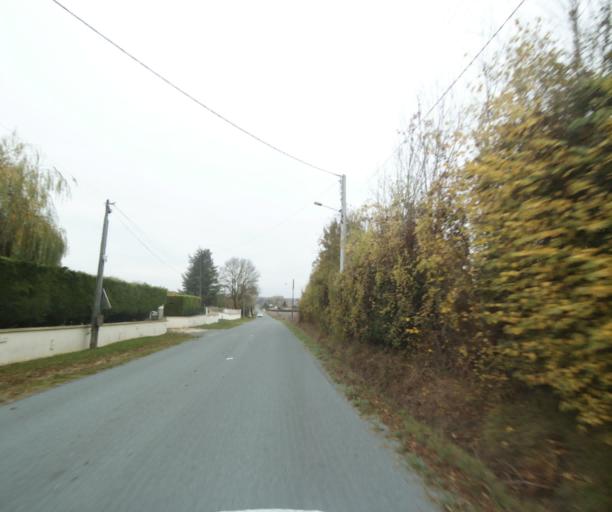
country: FR
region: Poitou-Charentes
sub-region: Departement de la Charente-Maritime
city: Chermignac
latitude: 45.7257
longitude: -0.6686
